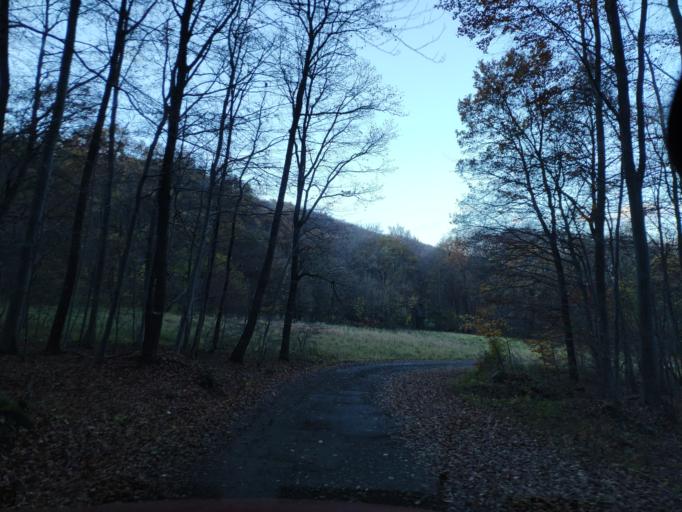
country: SK
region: Kosicky
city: Secovce
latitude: 48.5858
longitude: 21.5053
